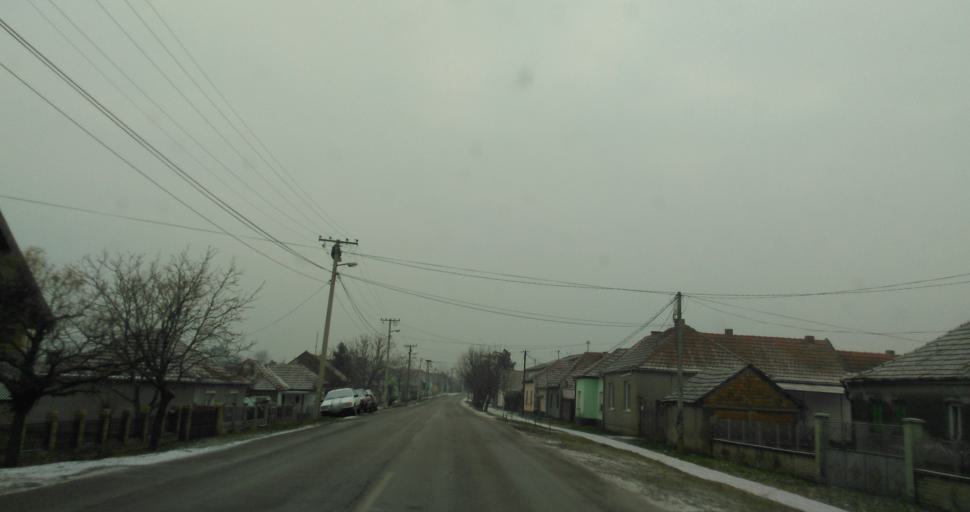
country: RS
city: Melenci
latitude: 45.5102
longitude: 20.3026
